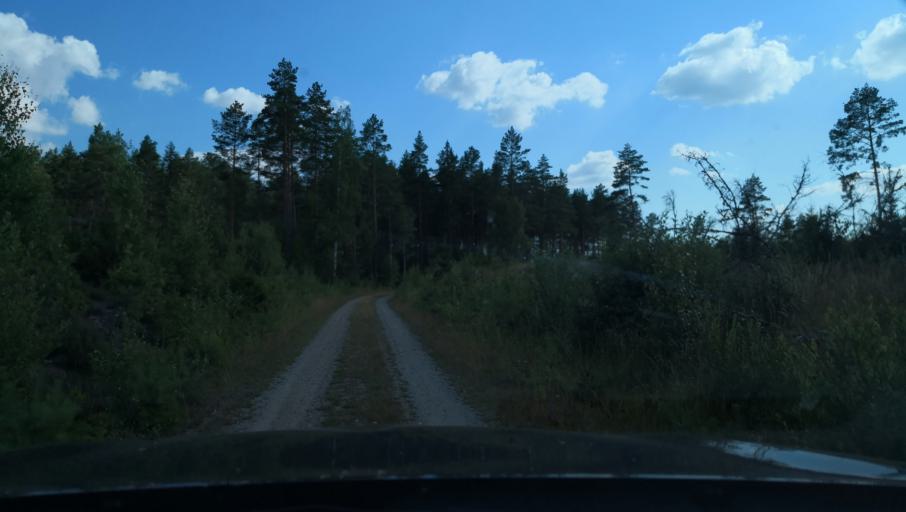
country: SE
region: Vaestmanland
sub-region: Vasteras
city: Skultuna
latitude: 59.7213
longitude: 16.3841
